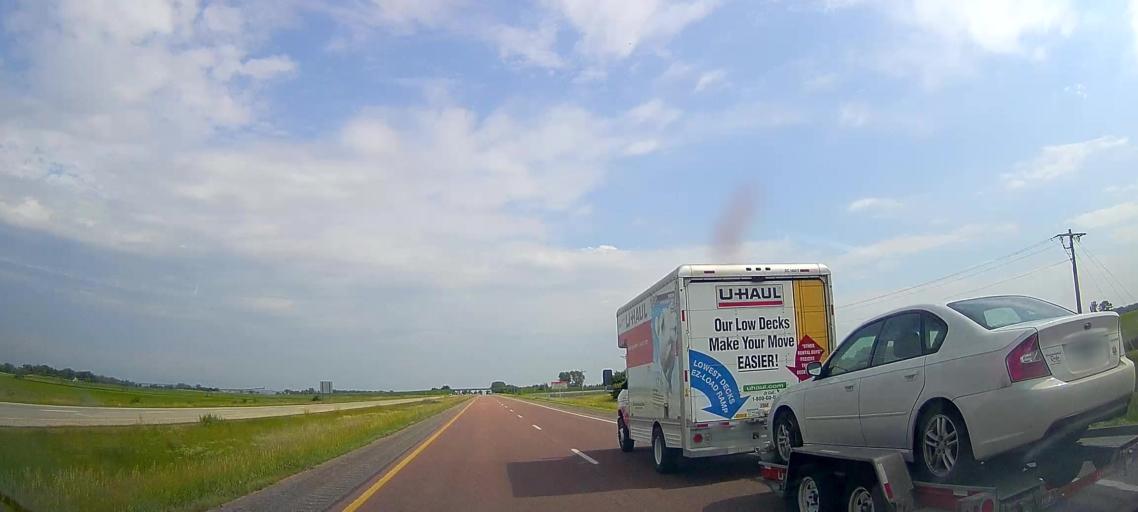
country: US
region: Iowa
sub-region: Monona County
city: Onawa
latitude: 41.9868
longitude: -96.1076
